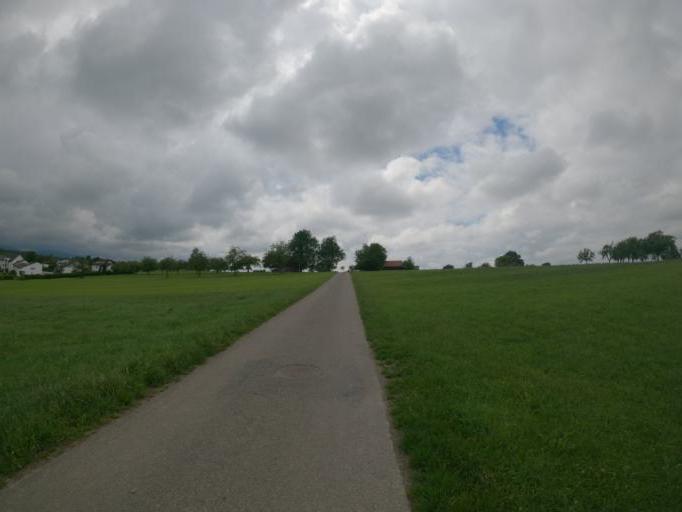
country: DE
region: Baden-Wuerttemberg
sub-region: Regierungsbezirk Stuttgart
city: Hattenhofen
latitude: 48.6727
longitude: 9.5704
